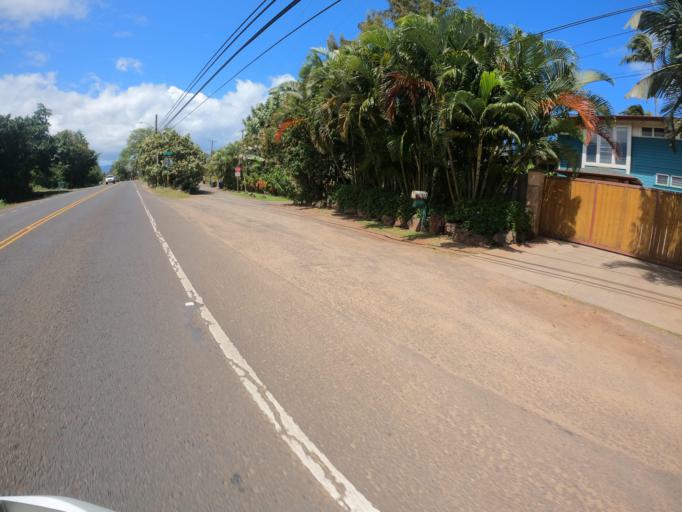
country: US
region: Hawaii
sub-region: Honolulu County
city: Pupukea
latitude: 21.6208
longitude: -158.0830
